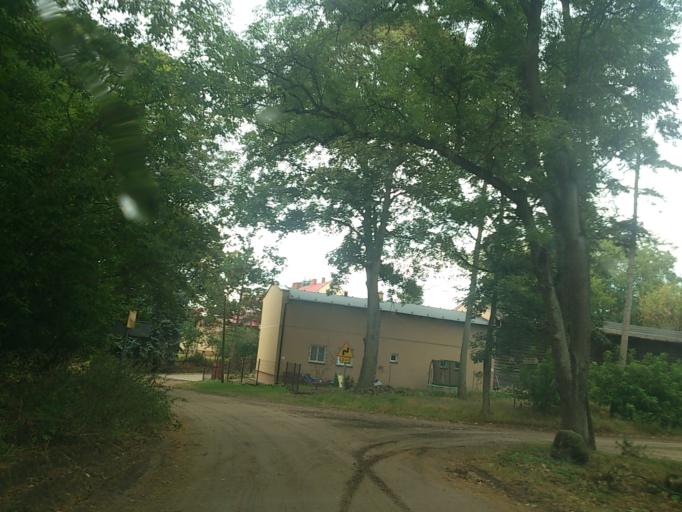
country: PL
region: Greater Poland Voivodeship
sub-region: Powiat poznanski
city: Murowana Goslina
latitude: 52.5539
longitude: 17.1131
